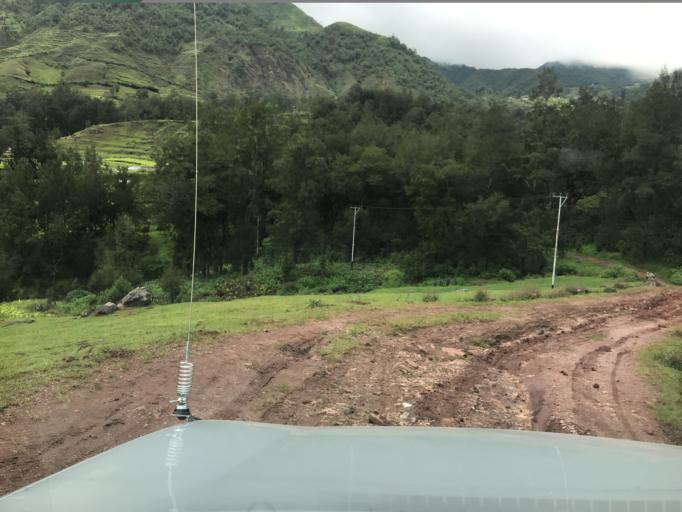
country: TL
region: Aileu
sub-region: Aileu Villa
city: Aileu
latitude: -8.8617
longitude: 125.5662
